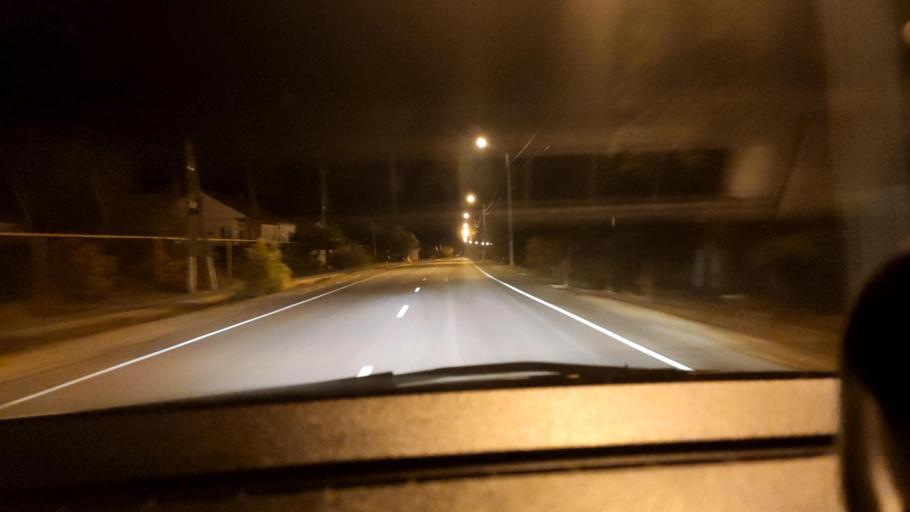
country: RU
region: Voronezj
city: Shilovo
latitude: 51.5627
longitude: 39.0550
